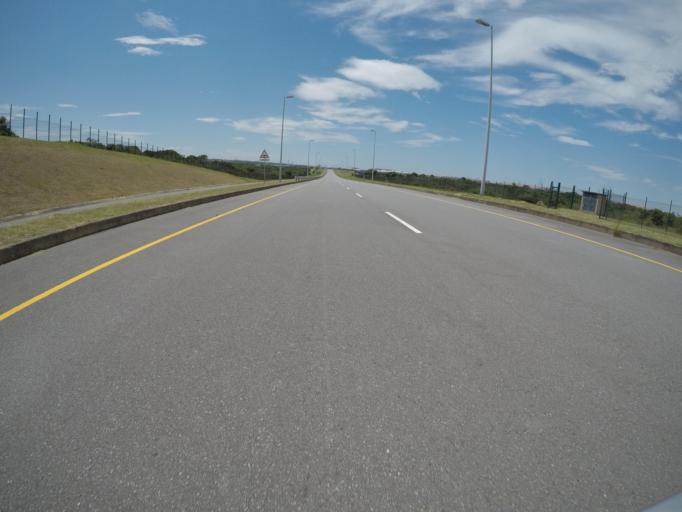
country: ZA
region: Eastern Cape
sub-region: Buffalo City Metropolitan Municipality
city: East London
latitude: -33.0549
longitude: 27.8401
